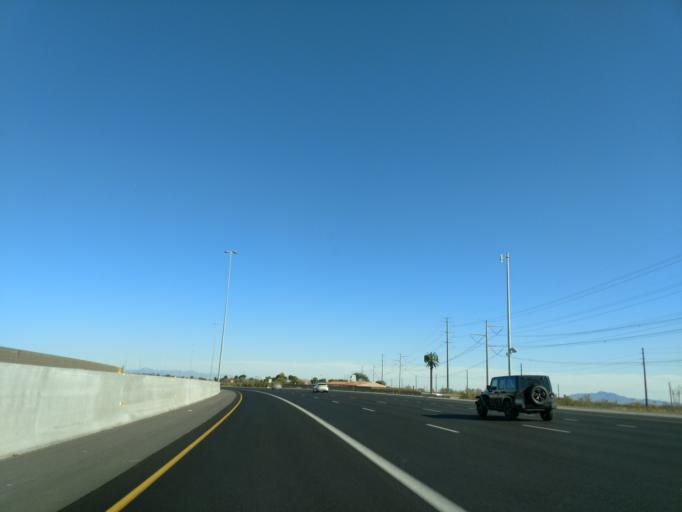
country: US
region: Arizona
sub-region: Maricopa County
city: Guadalupe
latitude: 33.2923
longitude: -111.9929
